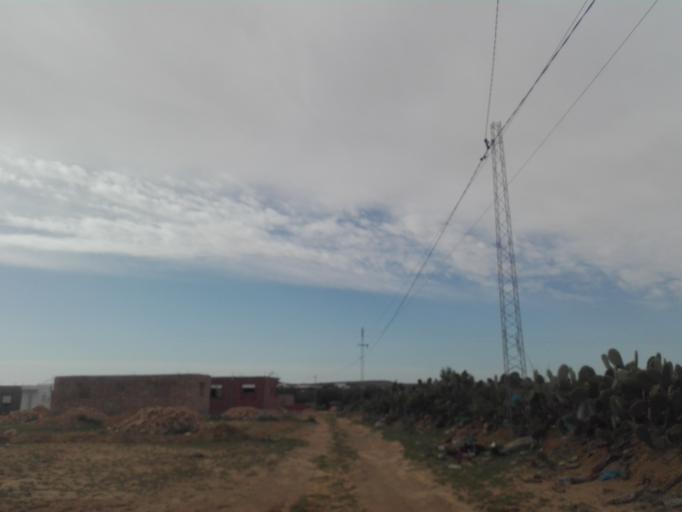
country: TN
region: Safaqis
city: Sfax
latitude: 34.7391
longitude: 10.5085
